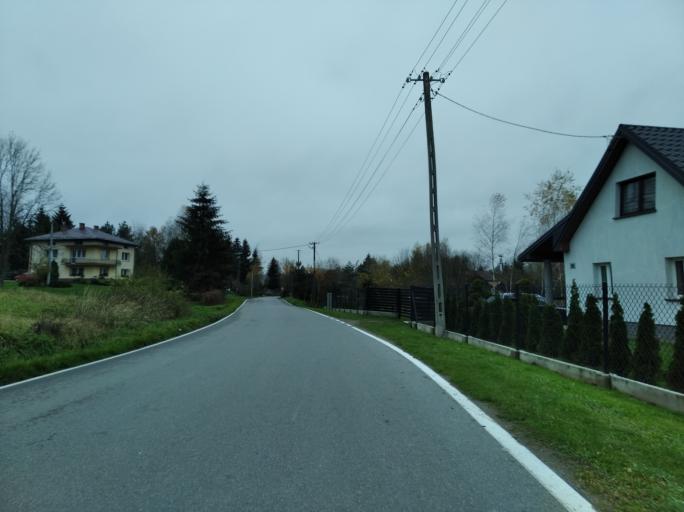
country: PL
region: Subcarpathian Voivodeship
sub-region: Powiat krosnienski
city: Leki
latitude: 49.8045
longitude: 21.6682
